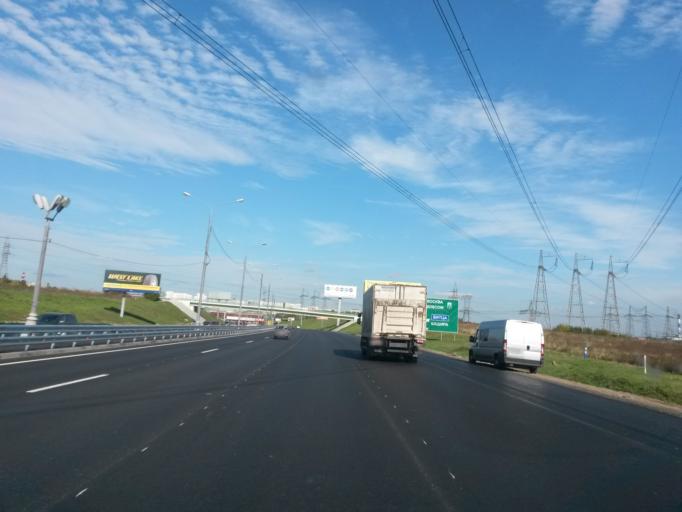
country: RU
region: Moscow
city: Annino
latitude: 55.5578
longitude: 37.6057
